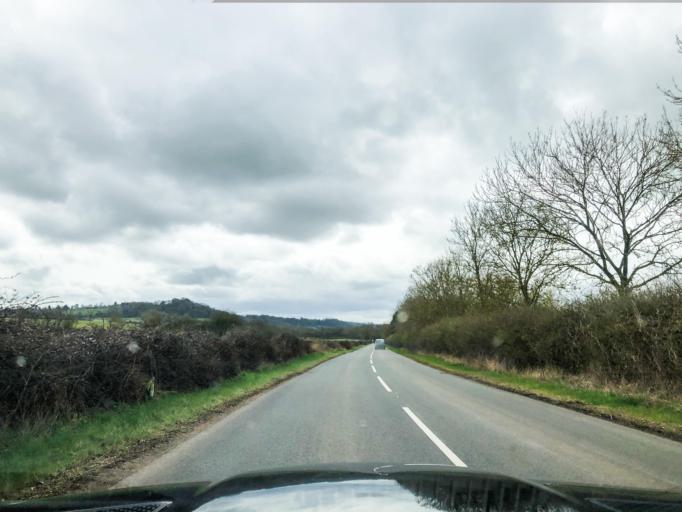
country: GB
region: England
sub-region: Warwickshire
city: Harbury
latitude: 52.1499
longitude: -1.4387
